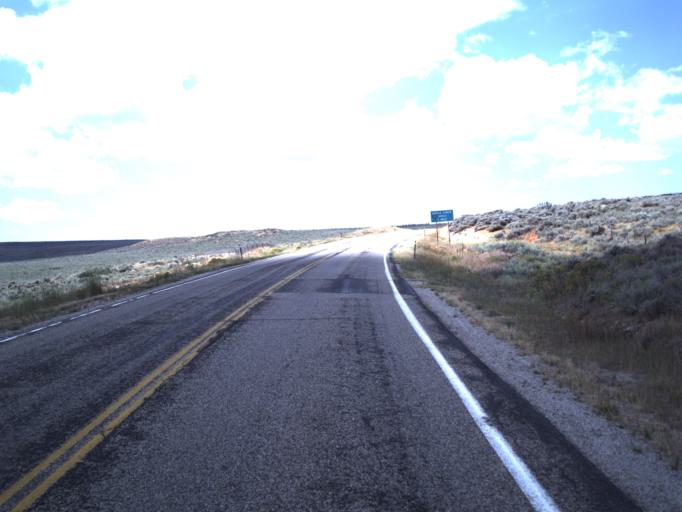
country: US
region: Utah
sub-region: Rich County
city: Randolph
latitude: 41.7951
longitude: -111.2315
